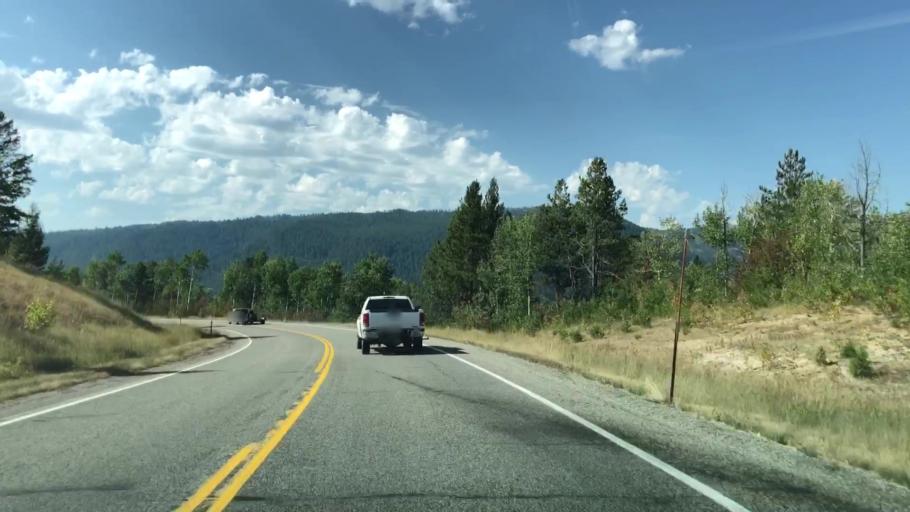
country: US
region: Wyoming
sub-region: Teton County
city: Hoback
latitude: 43.2537
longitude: -111.1168
